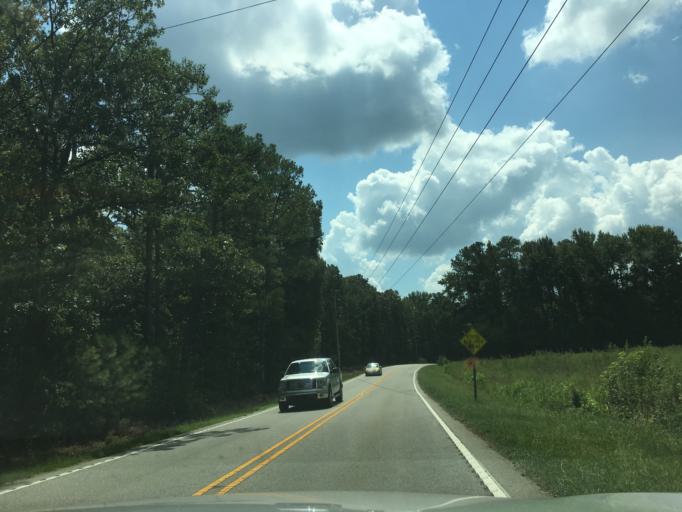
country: US
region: South Carolina
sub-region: Richland County
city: Lake Murray of Richland
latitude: 34.1337
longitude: -81.2166
